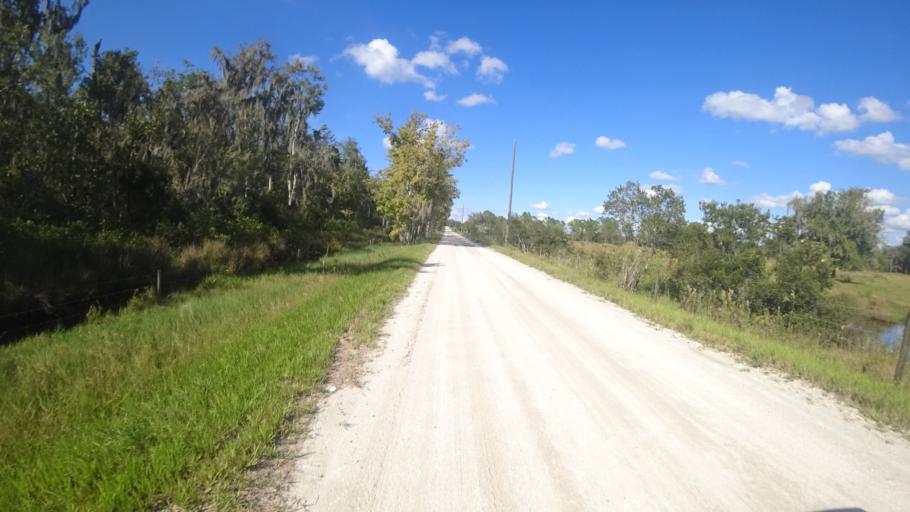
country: US
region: Florida
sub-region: Hardee County
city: Wauchula
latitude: 27.4660
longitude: -82.0554
